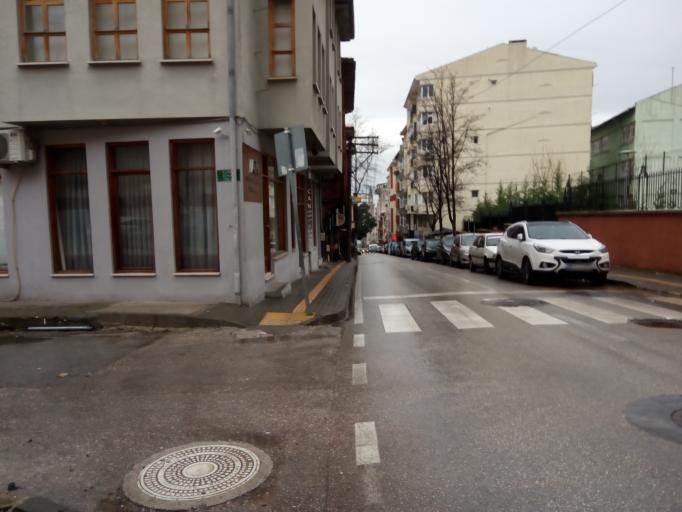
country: TR
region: Bursa
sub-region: Osmangazi
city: Bursa
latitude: 40.1801
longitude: 29.0618
